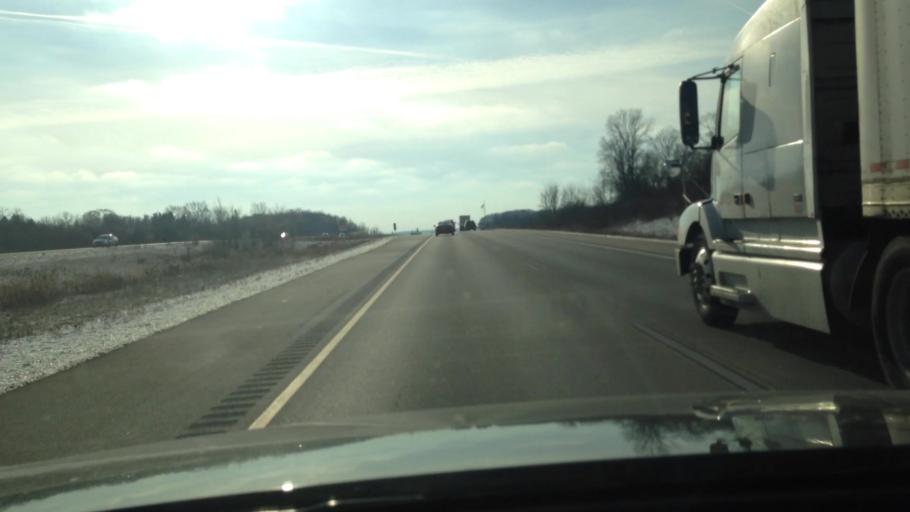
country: US
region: Wisconsin
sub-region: Waukesha County
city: Big Bend
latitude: 42.8887
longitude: -88.2703
